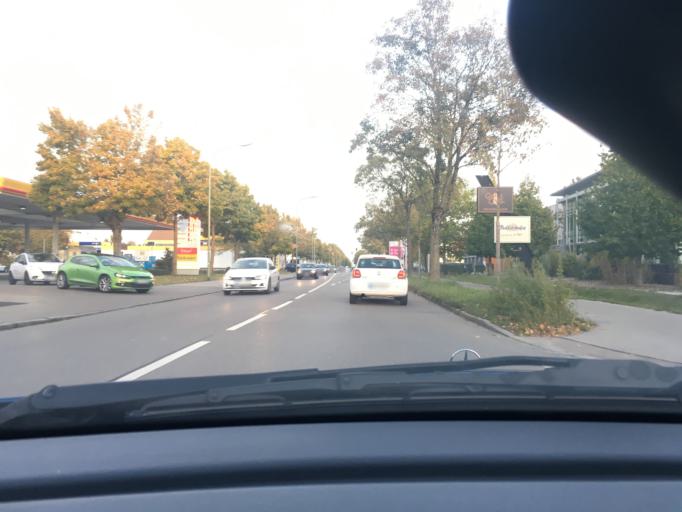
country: DE
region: Bavaria
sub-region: Swabia
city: Stadtbergen
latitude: 48.3860
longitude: 10.8479
